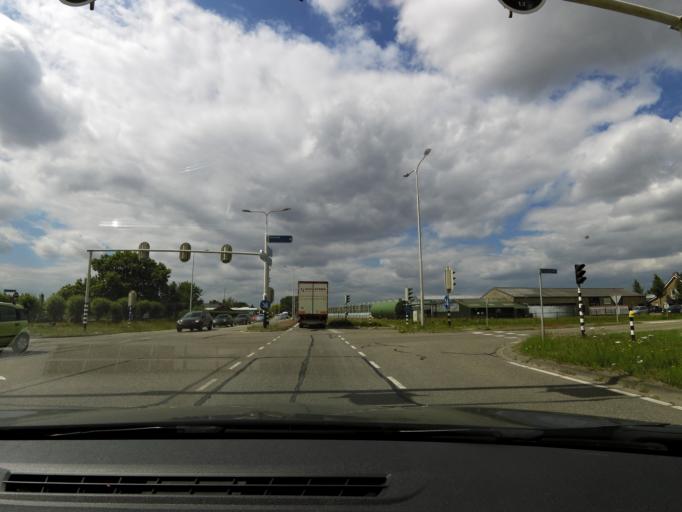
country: NL
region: North Brabant
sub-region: Gemeente Oosterhout
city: Oosterhout
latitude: 51.6413
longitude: 4.8926
